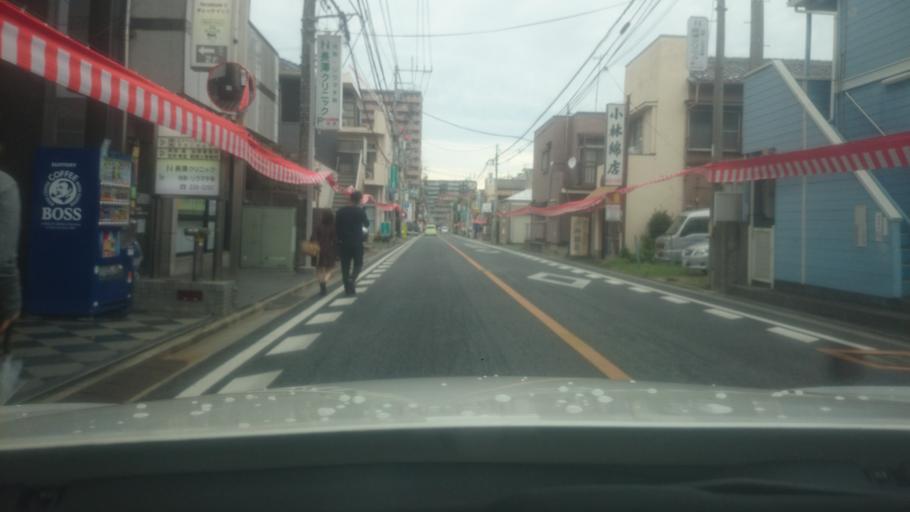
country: JP
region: Saitama
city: Kawagoe
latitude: 35.9133
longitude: 139.4856
